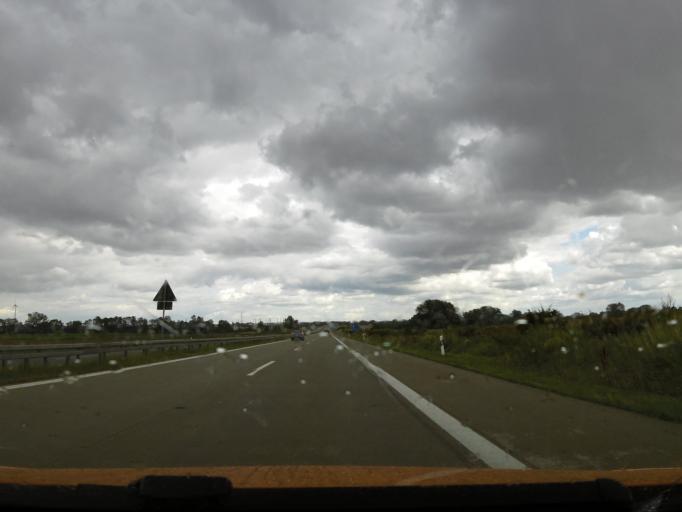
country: DE
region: Mecklenburg-Vorpommern
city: Penkun
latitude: 53.3120
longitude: 14.2518
